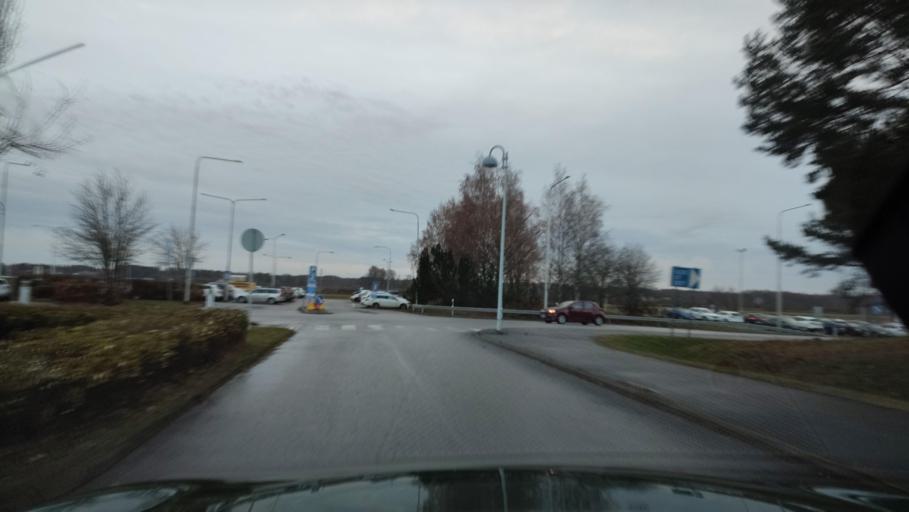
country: FI
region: Ostrobothnia
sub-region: Vaasa
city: Ristinummi
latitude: 63.0435
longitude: 21.7591
